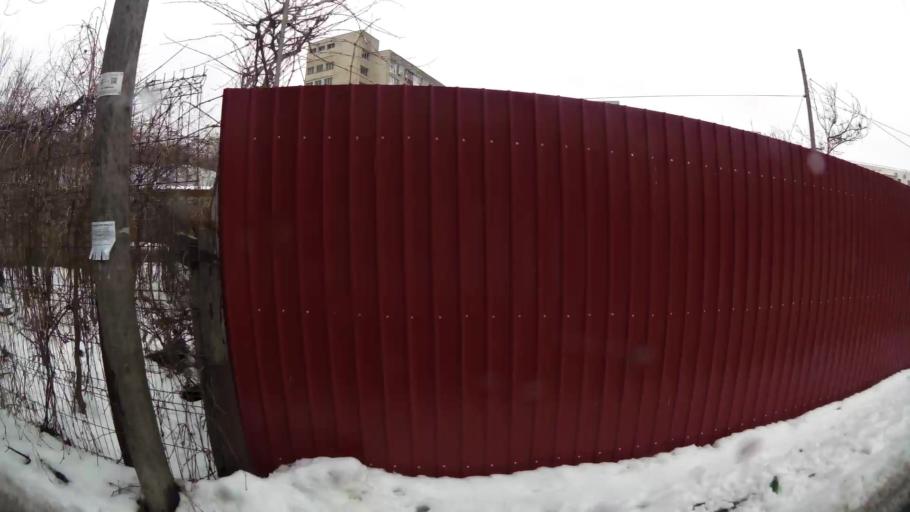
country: RO
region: Ilfov
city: Dobroesti
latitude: 44.4344
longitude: 26.1660
